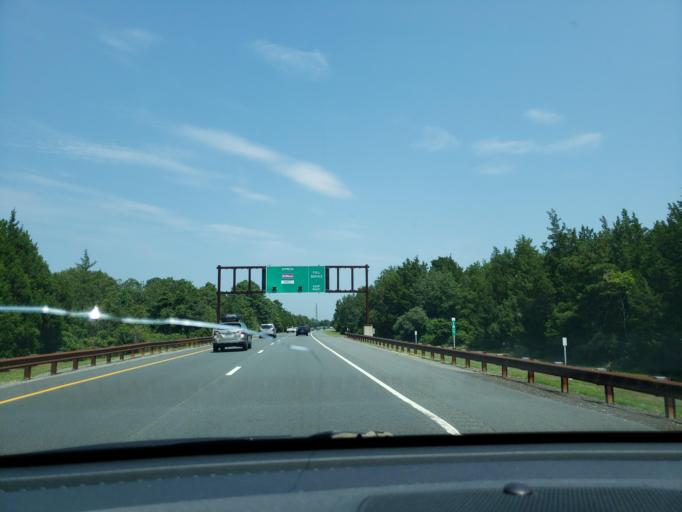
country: US
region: New Jersey
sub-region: Cape May County
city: Sea Isle City
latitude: 39.1861
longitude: -74.7180
